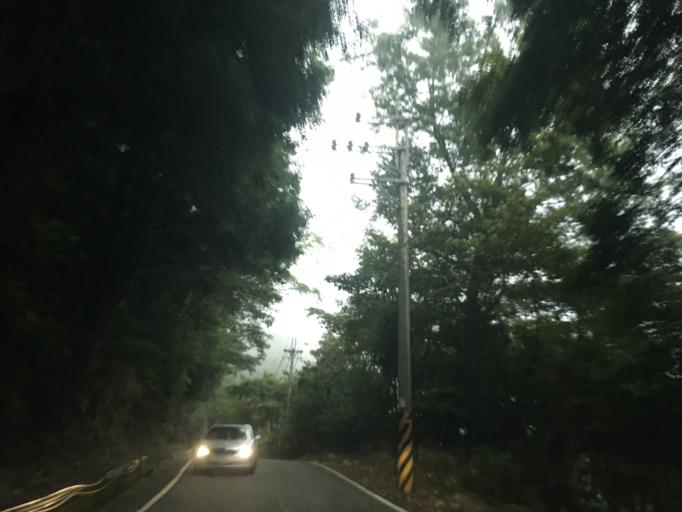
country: TW
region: Taiwan
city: Fengyuan
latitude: 24.2450
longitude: 120.9314
